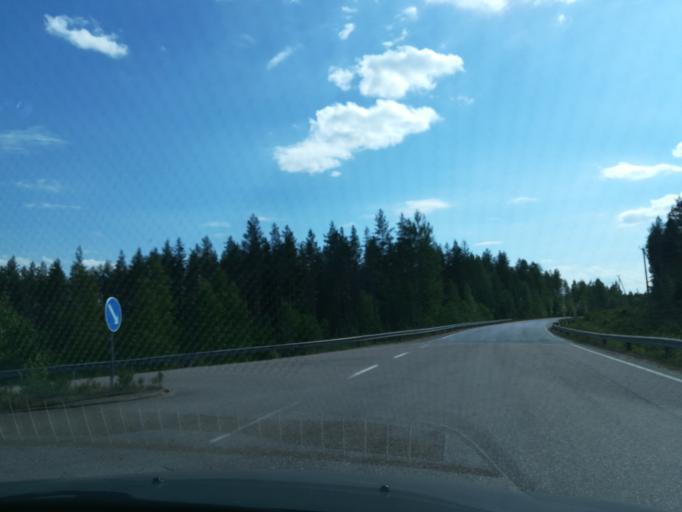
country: FI
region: South Karelia
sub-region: Imatra
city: Ruokolahti
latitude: 61.4743
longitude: 28.7902
